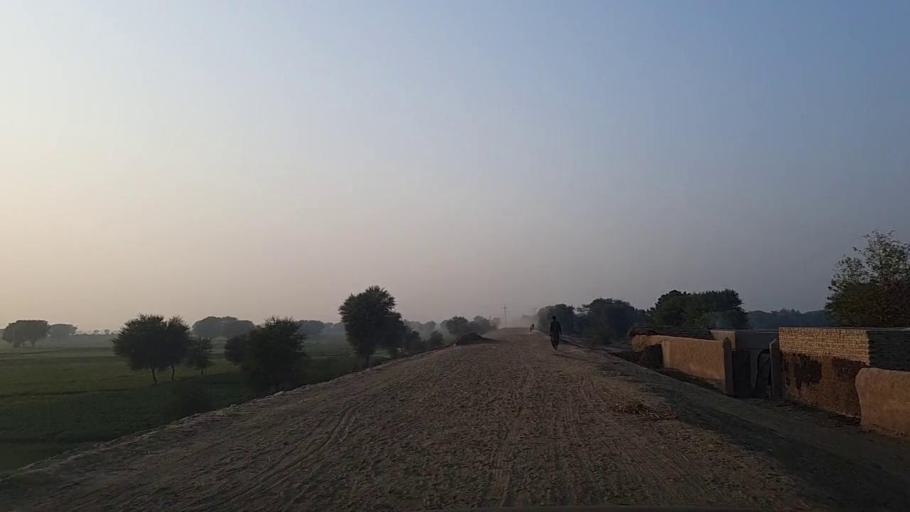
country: PK
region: Sindh
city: Sann
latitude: 26.1730
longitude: 68.1027
